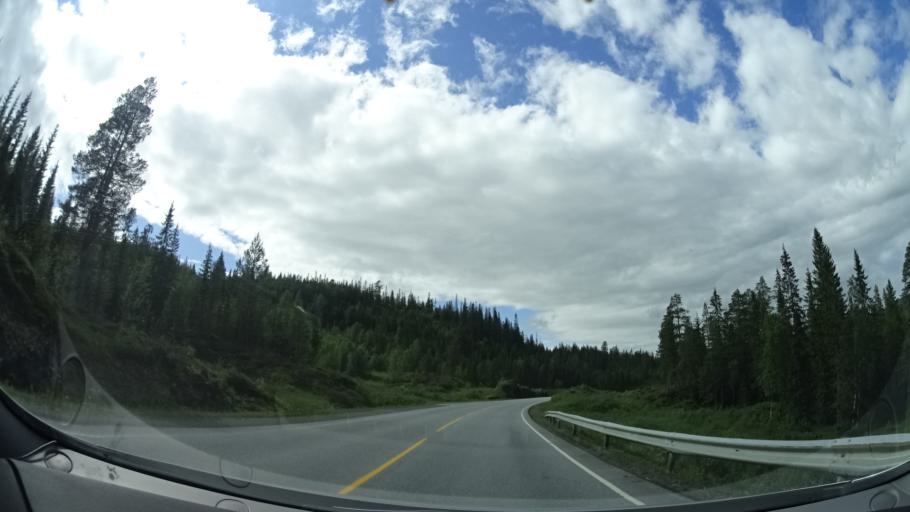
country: NO
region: Nord-Trondelag
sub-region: Meraker
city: Meraker
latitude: 63.3814
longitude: 11.8585
